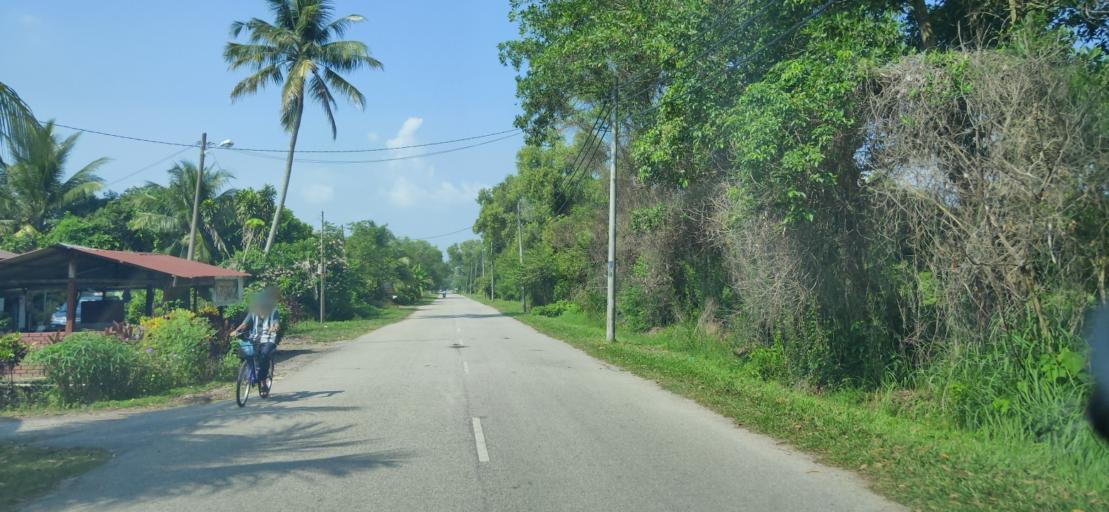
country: MY
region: Kedah
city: Sungai Petani
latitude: 5.6703
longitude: 100.4616
